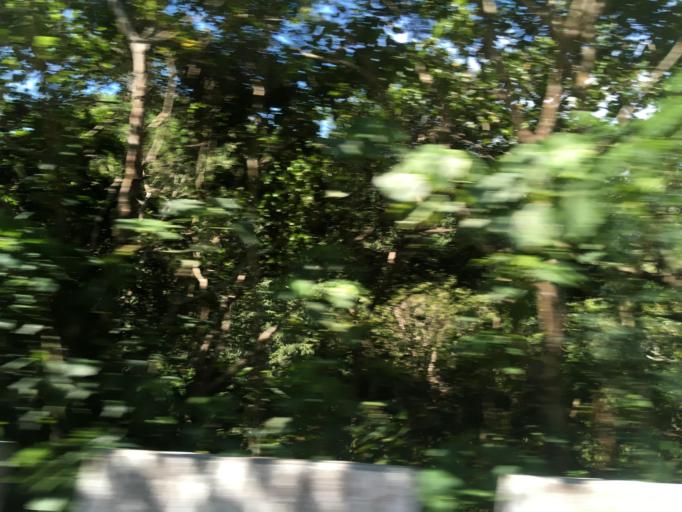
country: TW
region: Taiwan
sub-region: Yilan
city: Yilan
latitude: 24.4348
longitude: 121.7509
